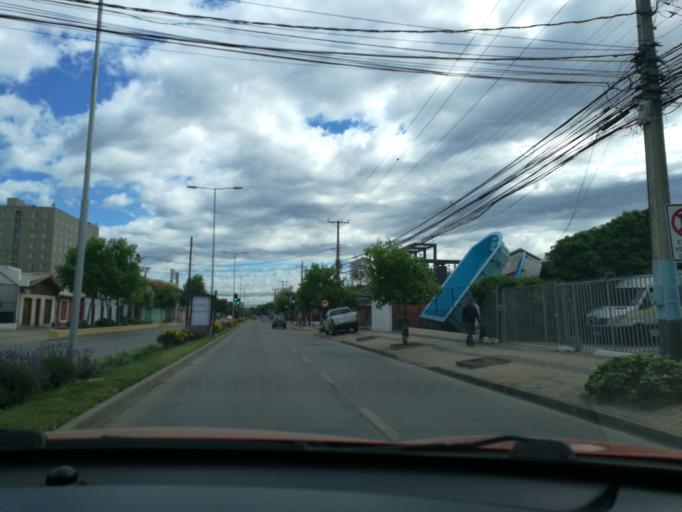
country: CL
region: O'Higgins
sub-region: Provincia de Cachapoal
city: Rancagua
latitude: -34.1687
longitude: -70.7347
